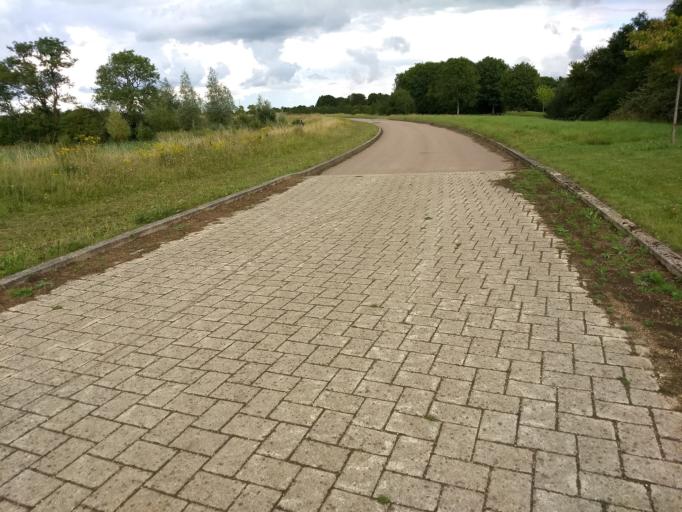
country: GB
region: England
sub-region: Buckinghamshire
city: Newton Longville
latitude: 51.9892
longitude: -0.7998
